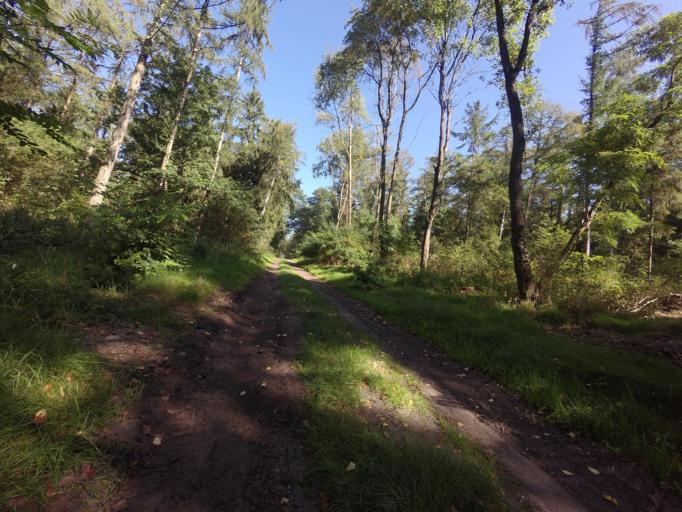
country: DE
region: Lower Saxony
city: Wielen
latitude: 52.5403
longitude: 6.7171
